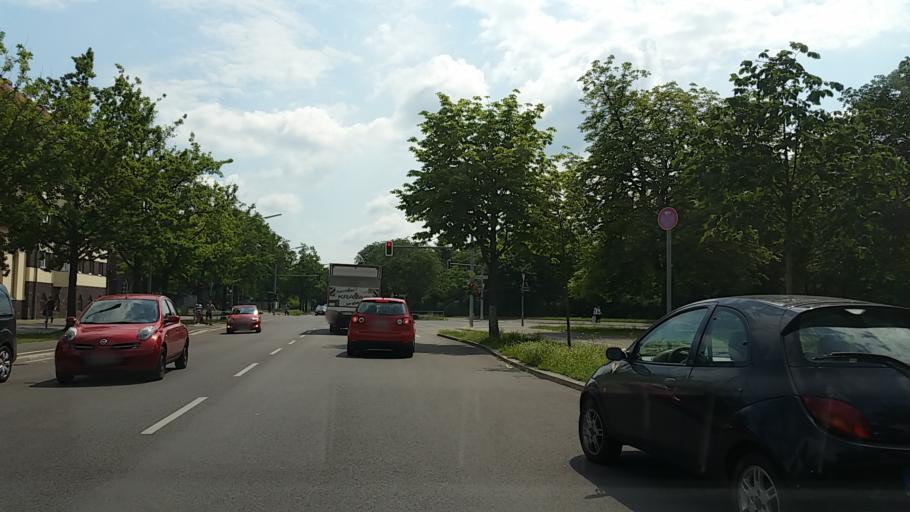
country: DE
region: Berlin
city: Spandau
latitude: 52.5497
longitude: 13.1933
